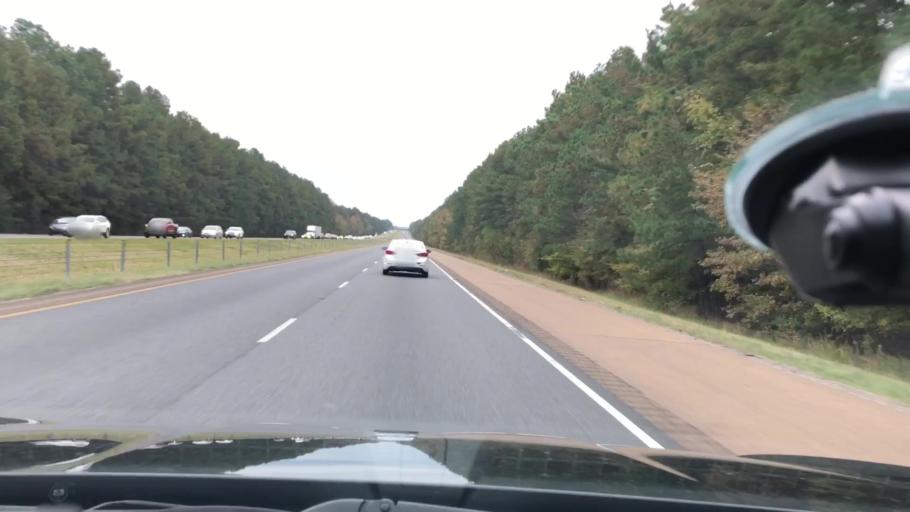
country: US
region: Arkansas
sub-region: Clark County
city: Gurdon
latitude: 33.9603
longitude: -93.2198
